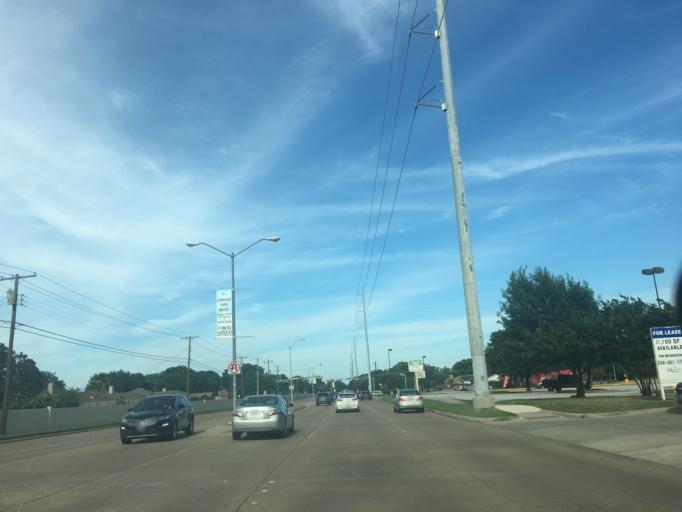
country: US
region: Texas
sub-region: Dallas County
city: Richardson
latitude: 32.9453
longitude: -96.6934
